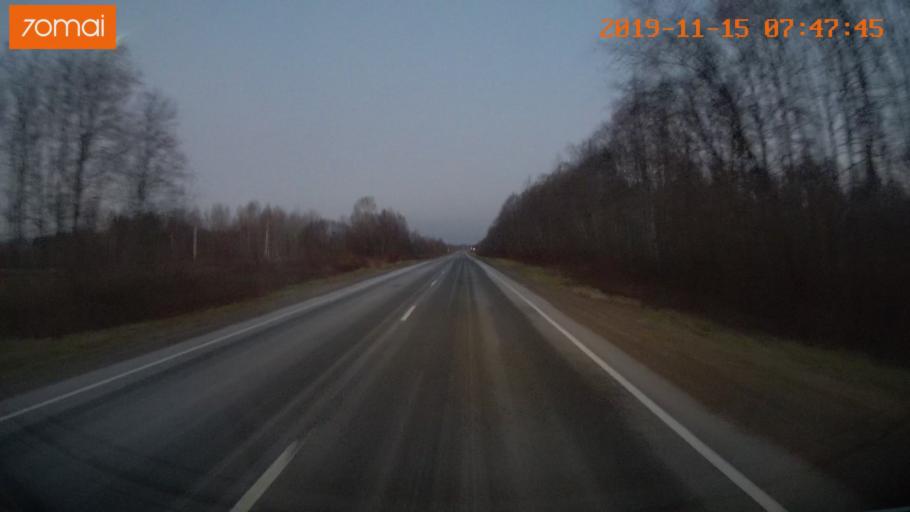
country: RU
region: Vologda
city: Sheksna
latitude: 58.8444
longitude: 38.2553
